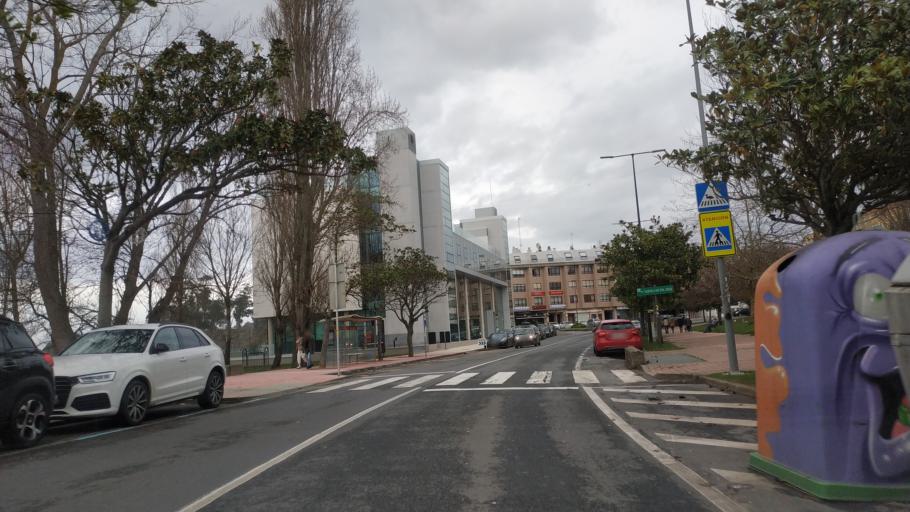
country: ES
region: Galicia
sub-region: Provincia da Coruna
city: Oleiros
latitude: 43.3480
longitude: -8.3462
